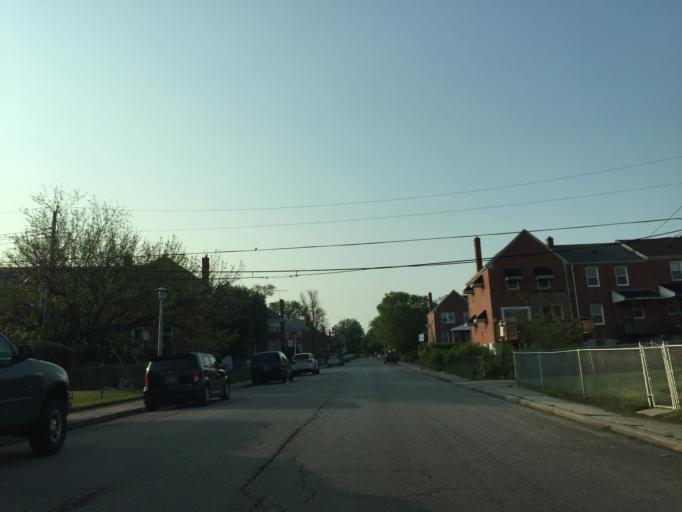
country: US
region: Maryland
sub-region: Baltimore County
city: Lochearn
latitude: 39.3335
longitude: -76.6707
